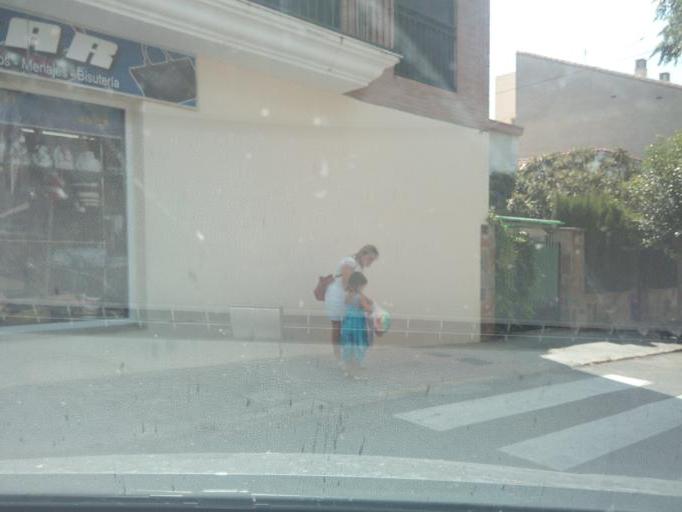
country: ES
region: Valencia
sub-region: Provincia de Valencia
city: Manises
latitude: 39.5265
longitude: -0.4870
